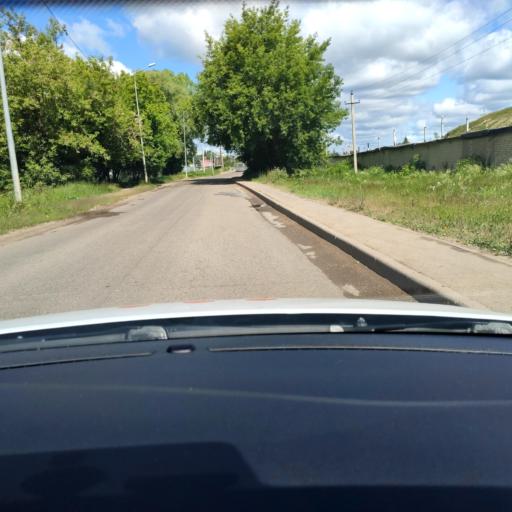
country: RU
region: Tatarstan
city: Vysokaya Gora
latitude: 55.8578
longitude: 49.2438
